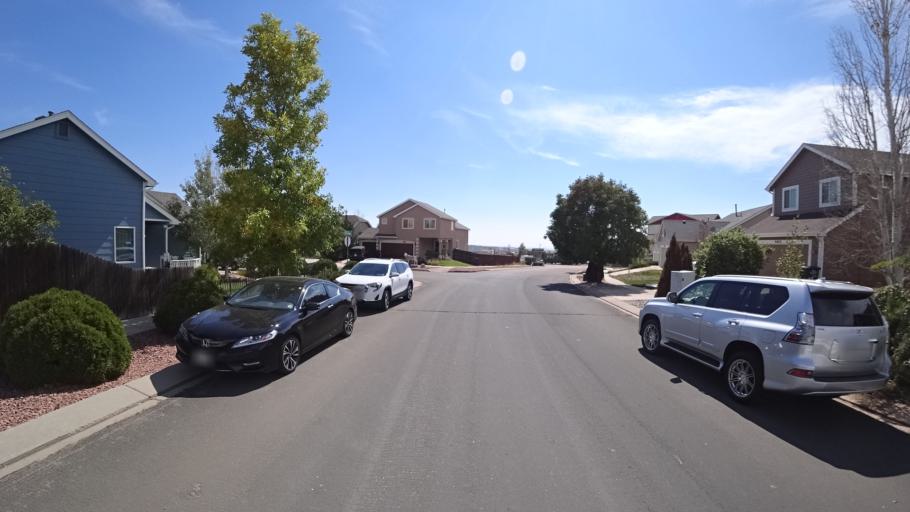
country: US
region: Colorado
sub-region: El Paso County
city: Cimarron Hills
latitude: 38.8979
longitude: -104.7141
